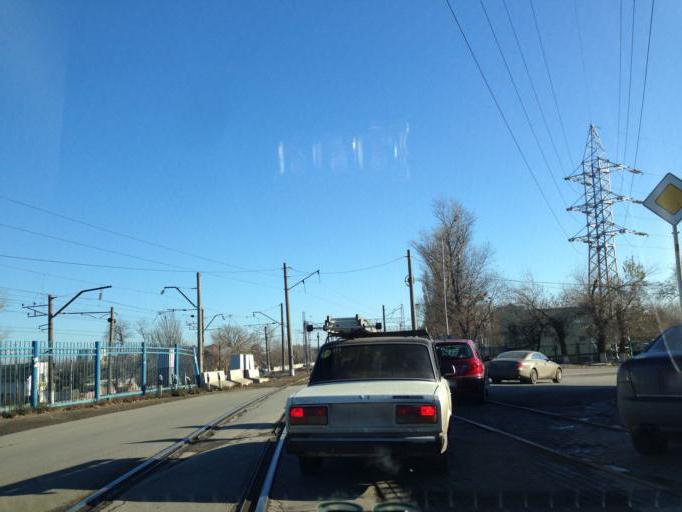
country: RU
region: Rostov
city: Rostov-na-Donu
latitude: 47.2437
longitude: 39.7325
